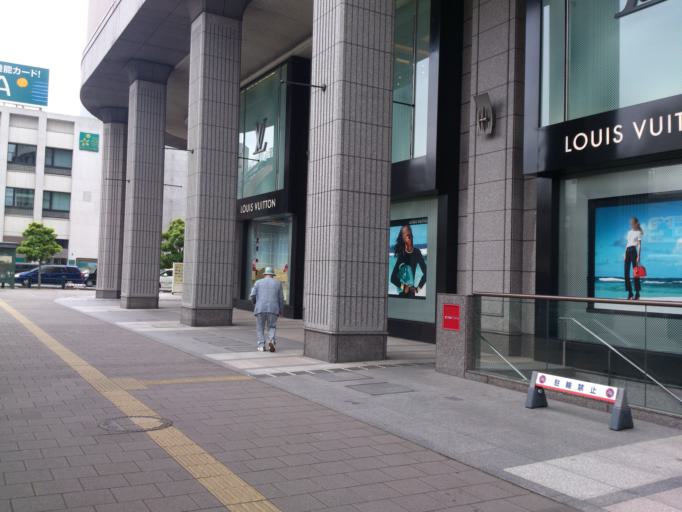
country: JP
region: Ehime
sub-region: Shikoku-chuo Shi
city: Matsuyama
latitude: 33.8364
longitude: 132.7631
